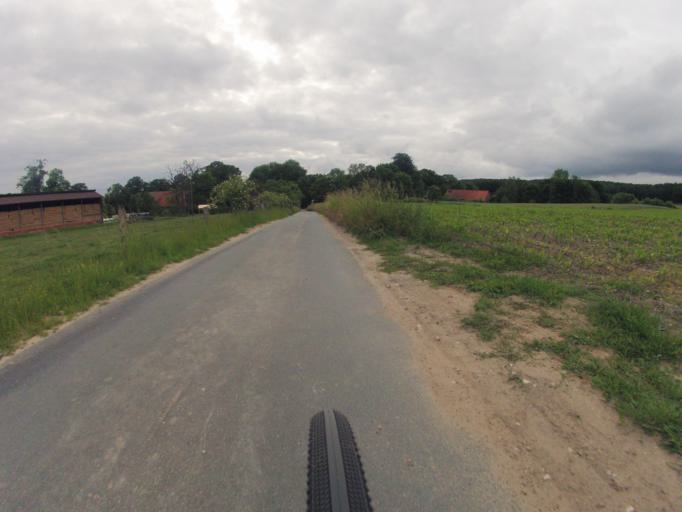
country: DE
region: North Rhine-Westphalia
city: Ibbenburen
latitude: 52.2388
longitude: 7.6984
